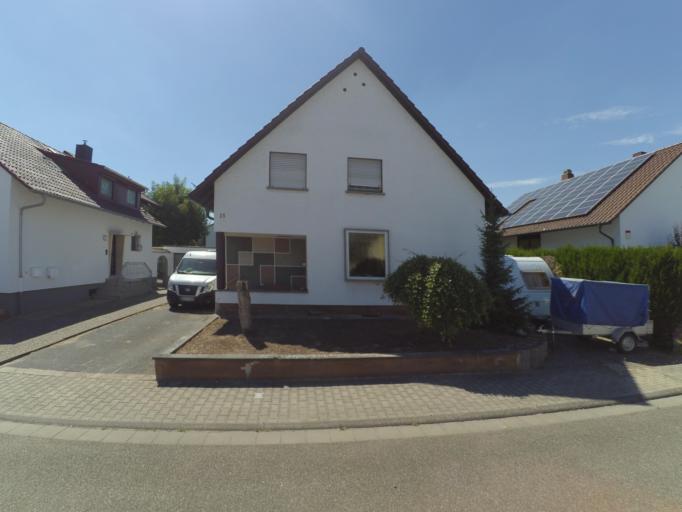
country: DE
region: Baden-Wuerttemberg
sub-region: Karlsruhe Region
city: Reilingen
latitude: 49.2914
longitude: 8.5609
